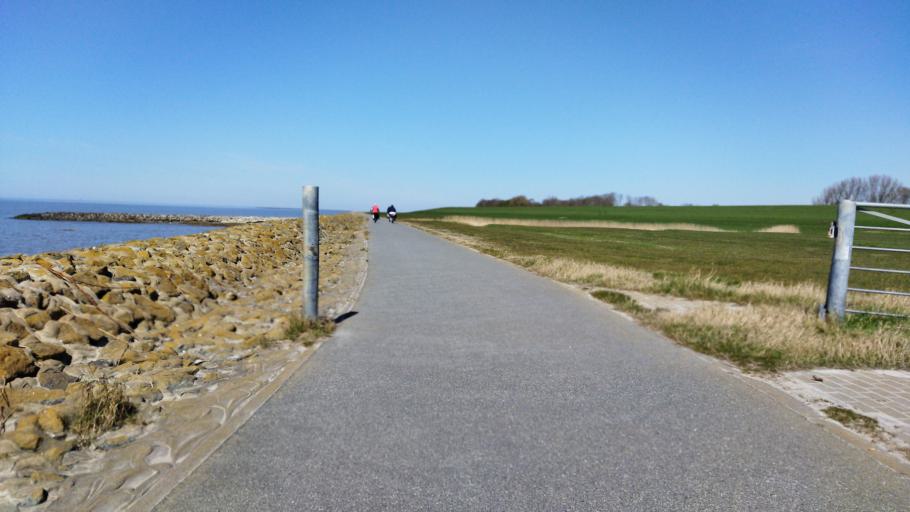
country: DE
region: Lower Saxony
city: Wremen
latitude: 53.6226
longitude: 8.5098
